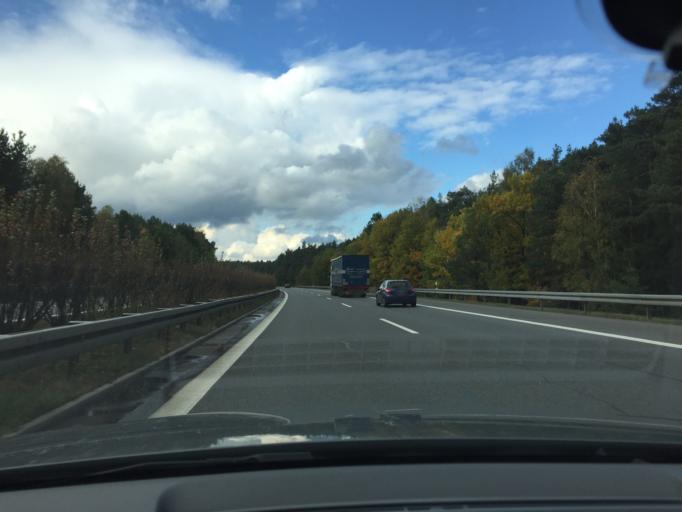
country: DE
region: Brandenburg
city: Bronkow
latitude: 51.6547
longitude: 13.9358
